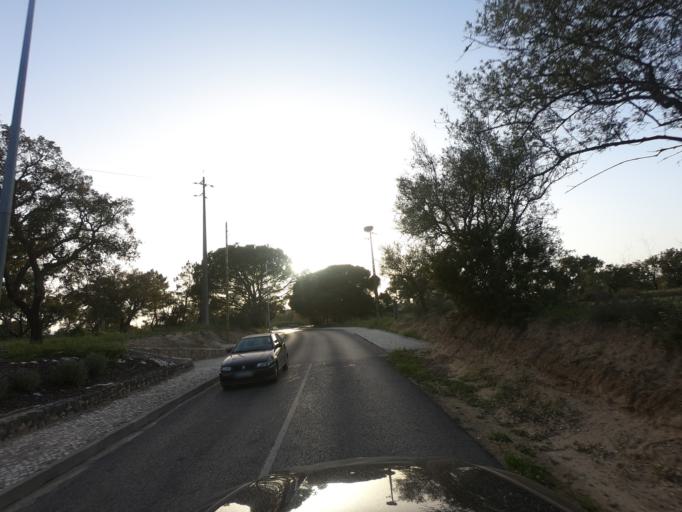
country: PT
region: Setubal
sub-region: Setubal
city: Setubal
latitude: 38.5376
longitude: -8.8269
